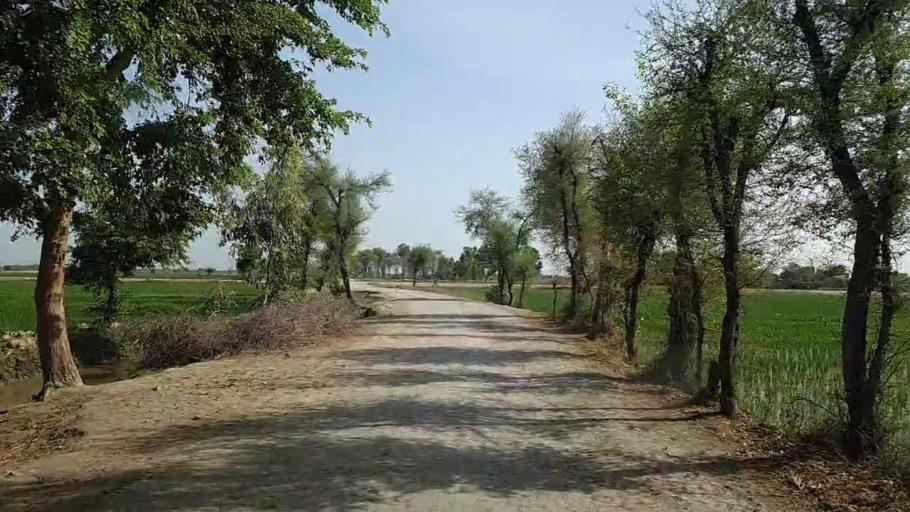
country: PK
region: Sindh
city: Sita Road
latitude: 27.0965
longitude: 67.8529
